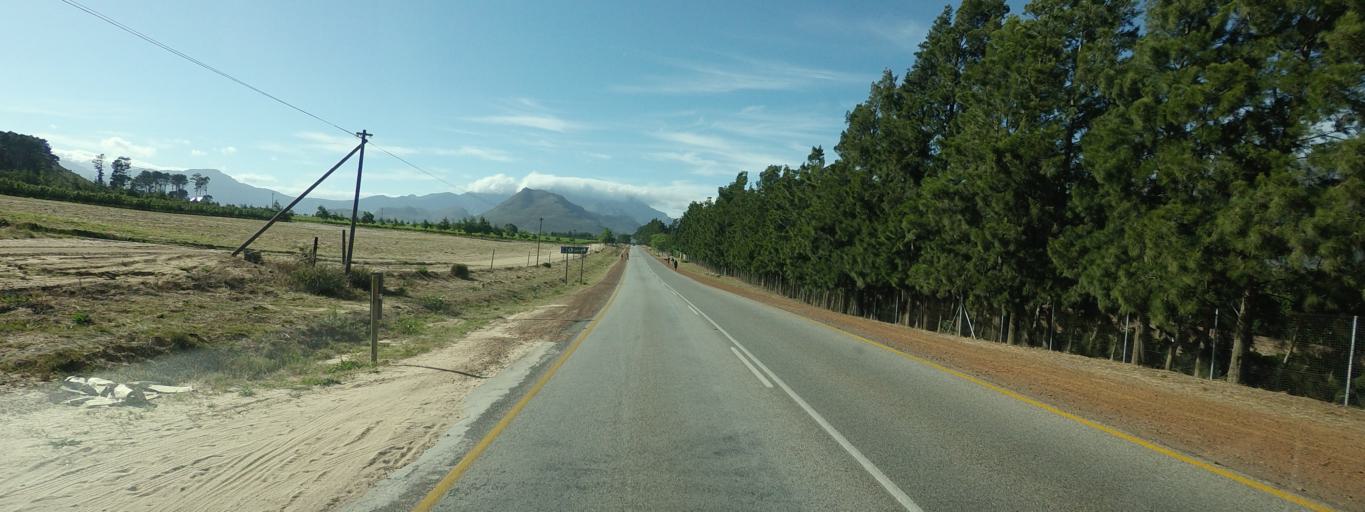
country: ZA
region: Western Cape
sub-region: Cape Winelands District Municipality
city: Paarl
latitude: -33.8637
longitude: 19.0399
